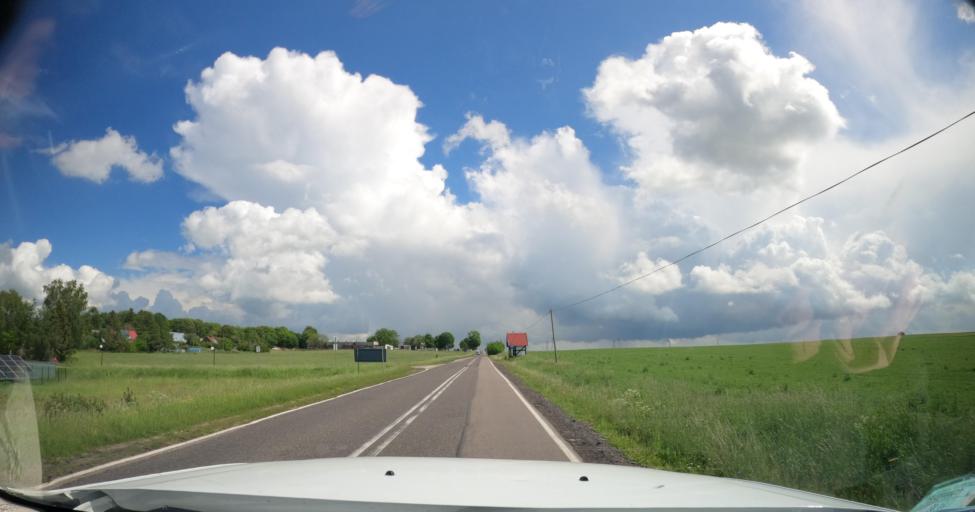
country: PL
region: Pomeranian Voivodeship
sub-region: Powiat bytowski
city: Czarna Dabrowka
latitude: 54.3664
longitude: 17.5058
